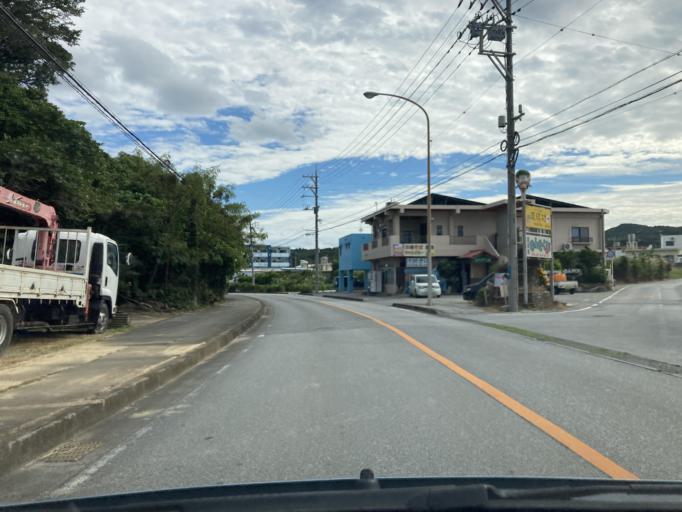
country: JP
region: Okinawa
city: Ishikawa
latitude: 26.4378
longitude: 127.7751
